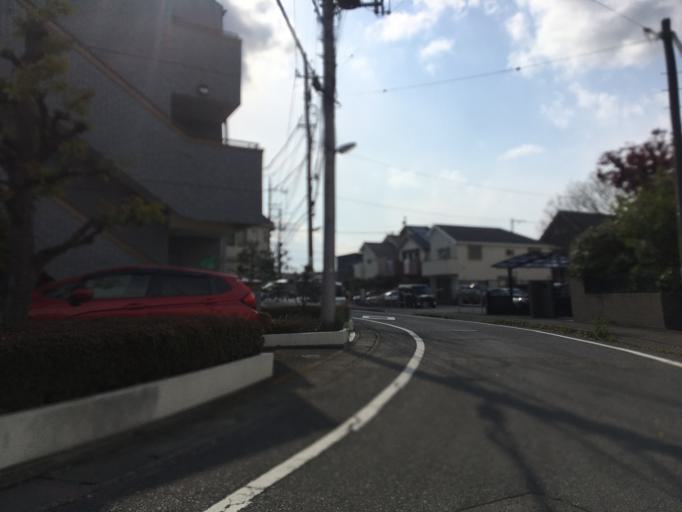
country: JP
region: Tokyo
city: Chofugaoka
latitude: 35.6418
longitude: 139.5056
